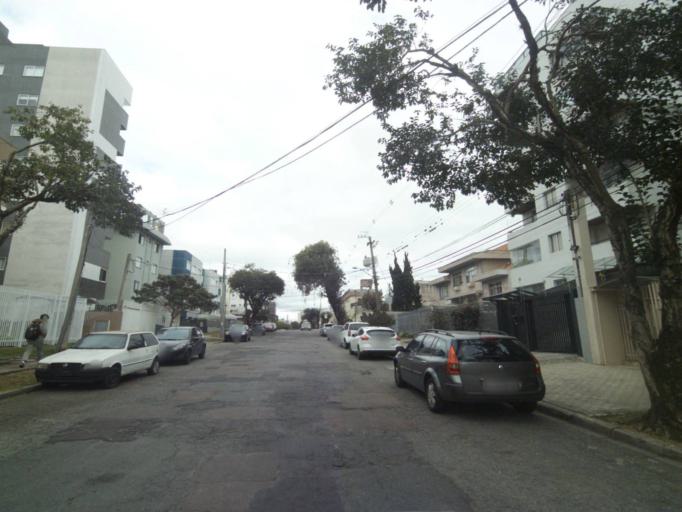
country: BR
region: Parana
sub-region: Curitiba
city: Curitiba
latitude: -25.4612
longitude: -49.2855
